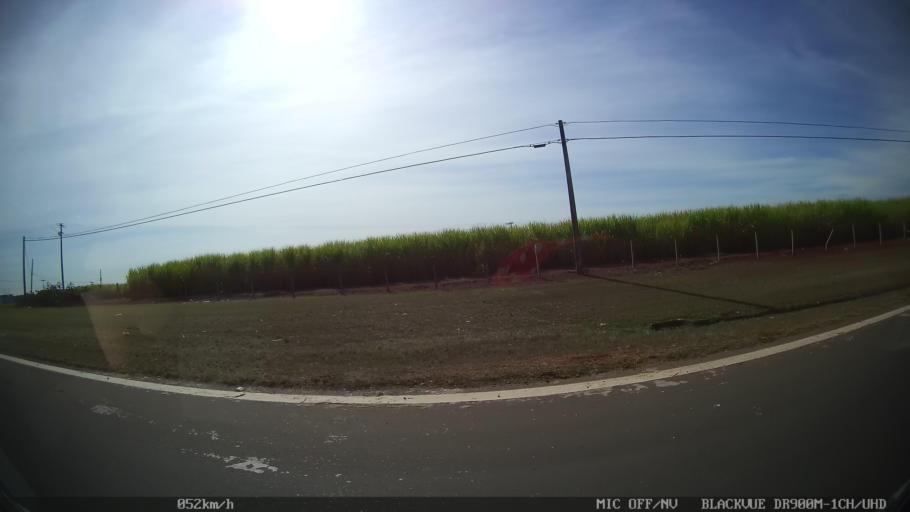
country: BR
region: Sao Paulo
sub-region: Piracicaba
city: Piracicaba
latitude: -22.7817
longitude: -47.6514
